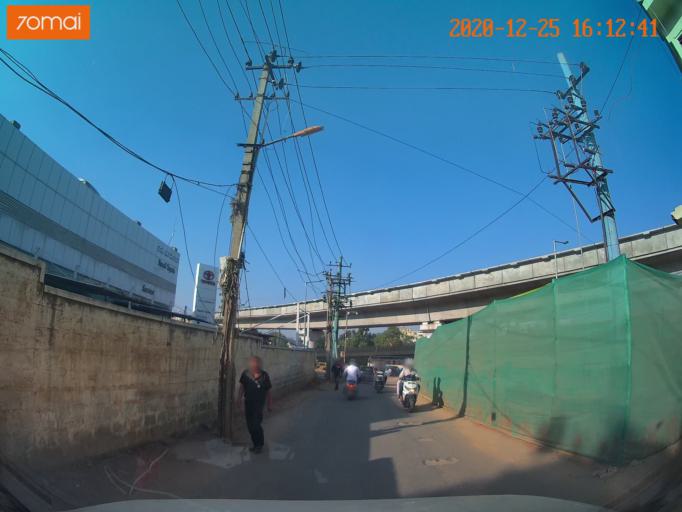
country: IN
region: Karnataka
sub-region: Bangalore Urban
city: Bangalore
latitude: 12.9077
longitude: 77.6279
